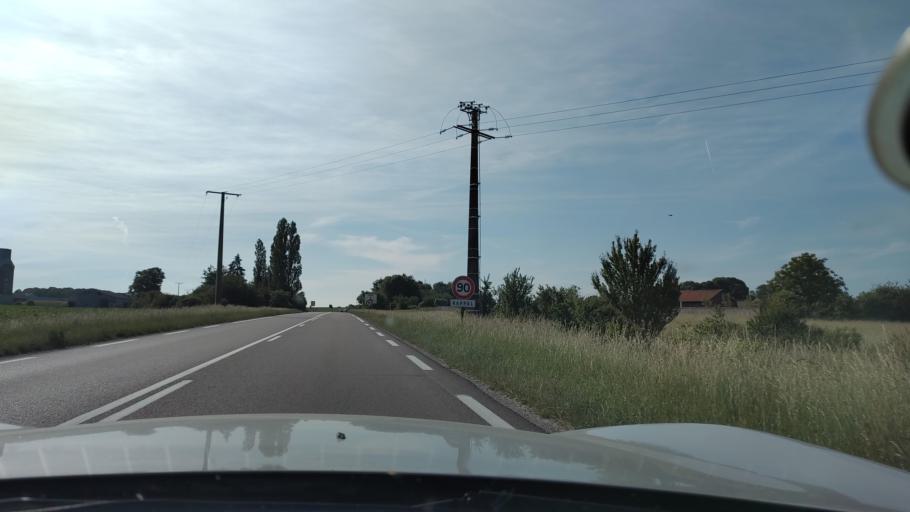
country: FR
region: Ile-de-France
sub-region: Departement de Seine-et-Marne
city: Jouy-le-Chatel
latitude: 48.6708
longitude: 3.1266
